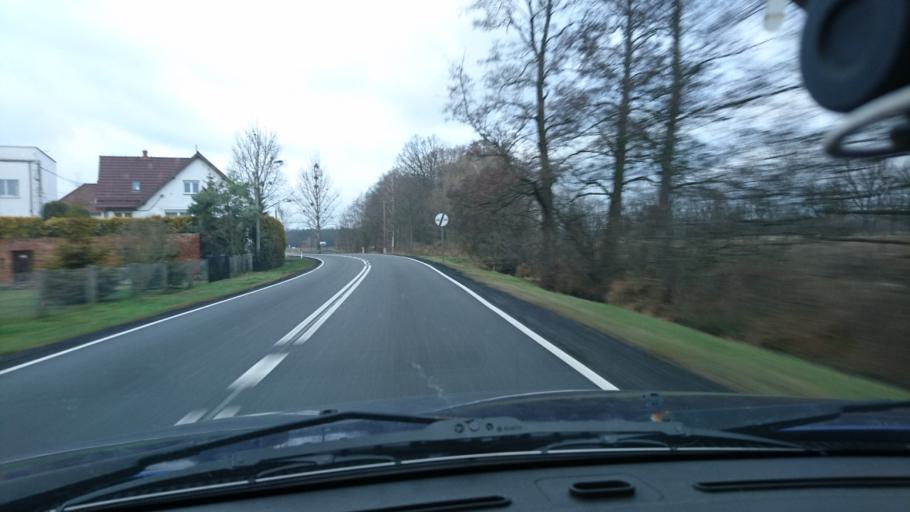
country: PL
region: Opole Voivodeship
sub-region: Powiat oleski
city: Olesno
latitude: 50.9159
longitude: 18.3469
